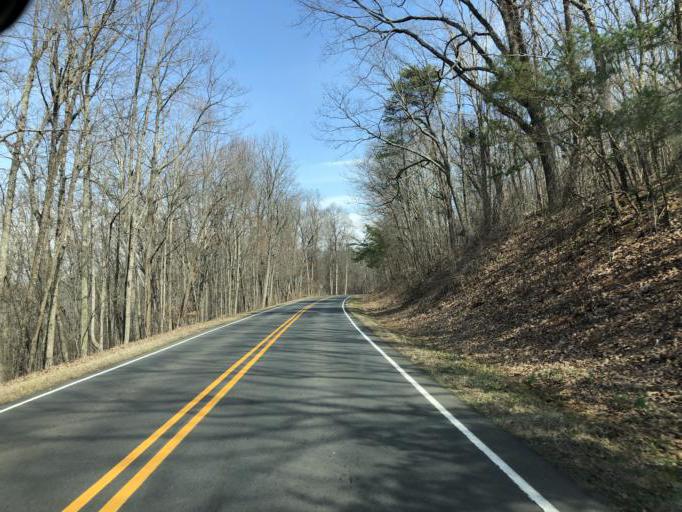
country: US
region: North Carolina
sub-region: Gaston County
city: Ranlo
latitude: 35.3019
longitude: -81.1174
